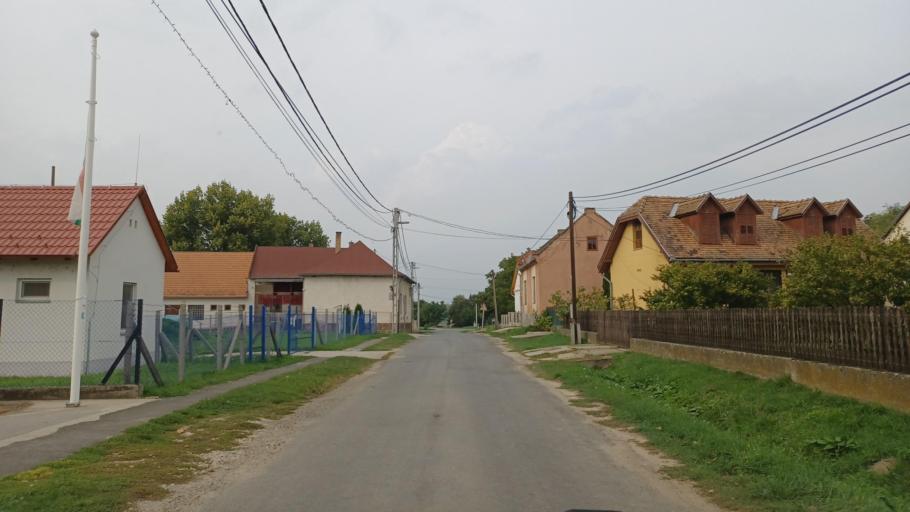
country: HU
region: Tolna
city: Gyonk
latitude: 46.5732
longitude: 18.4252
